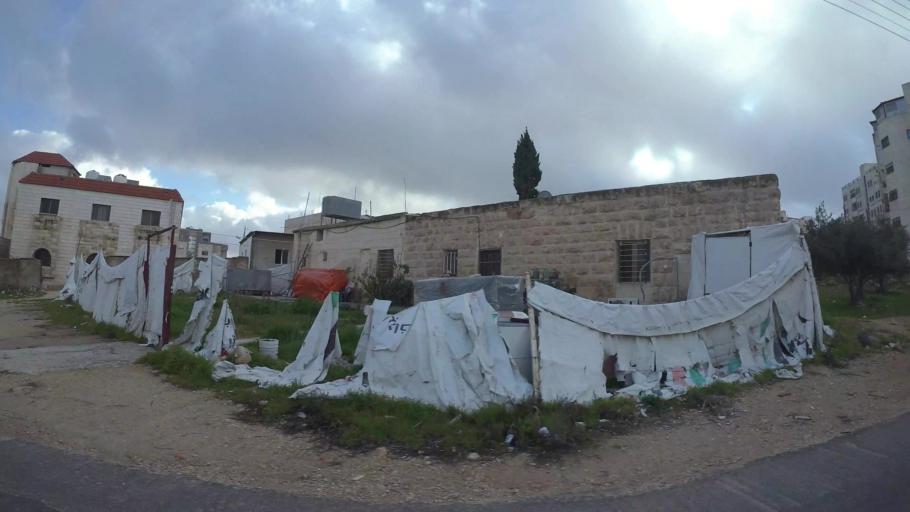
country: JO
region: Amman
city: Al Jubayhah
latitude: 32.0547
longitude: 35.8958
